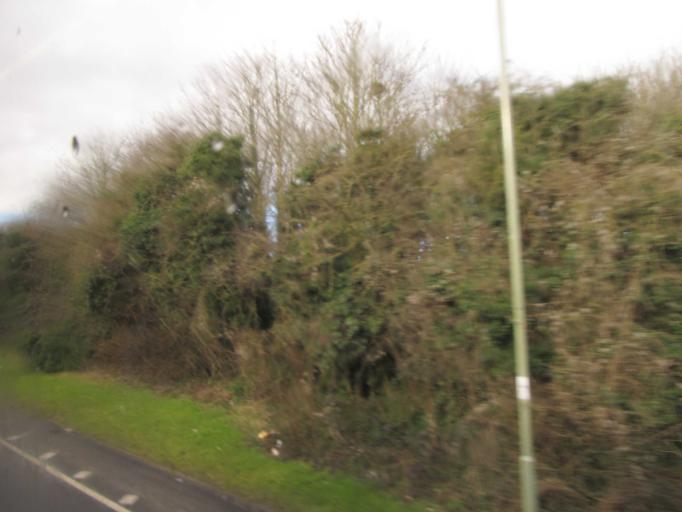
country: GB
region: England
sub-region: Hampshire
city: Basingstoke
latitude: 51.2370
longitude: -1.1389
